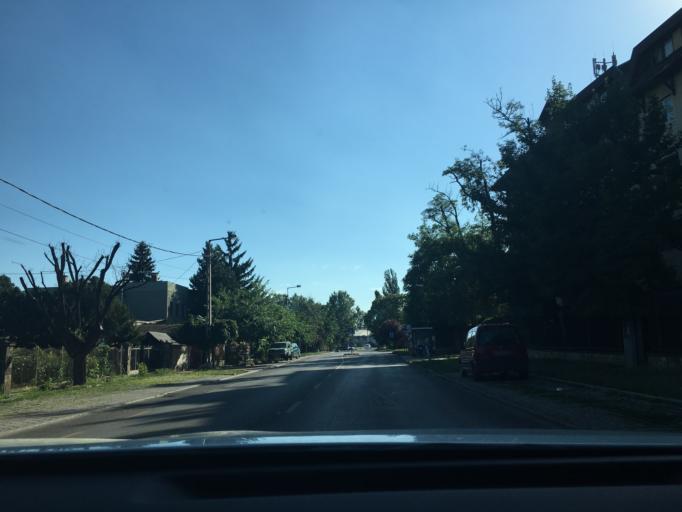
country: HU
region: Budapest
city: Budapest XVI. keruelet
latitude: 47.5071
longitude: 19.2057
